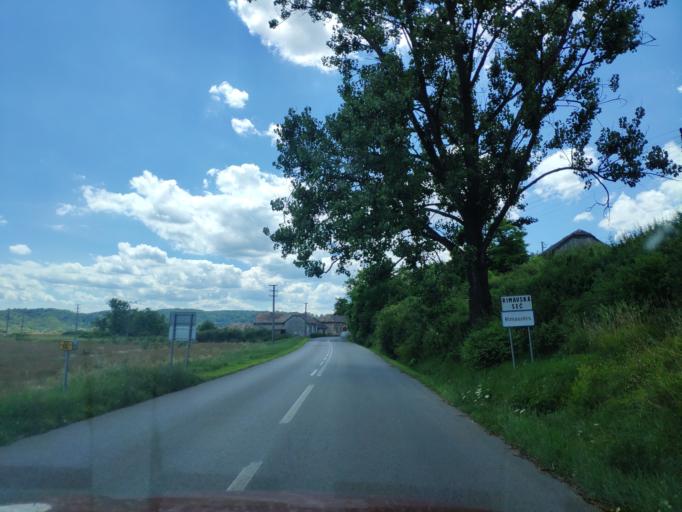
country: HU
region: Borsod-Abauj-Zemplen
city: Ozd
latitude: 48.3054
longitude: 20.2460
